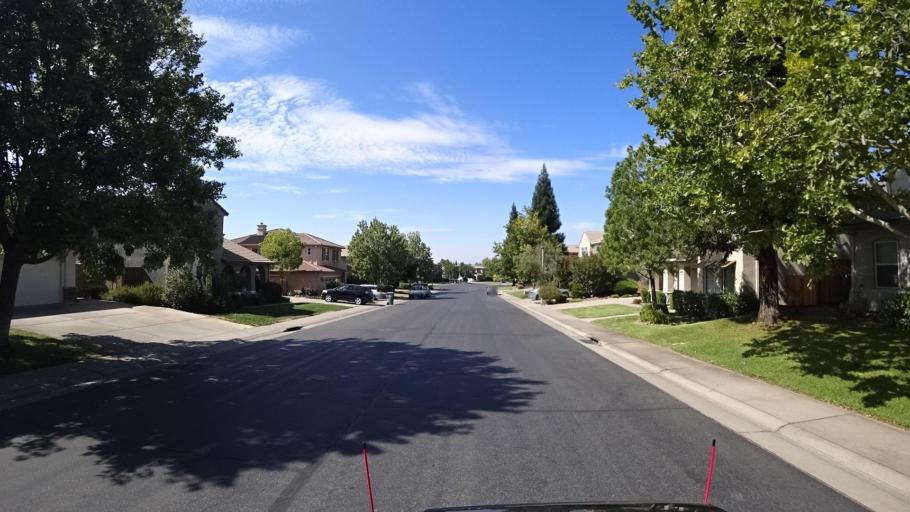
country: US
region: California
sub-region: Placer County
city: Roseville
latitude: 38.8039
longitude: -121.2863
